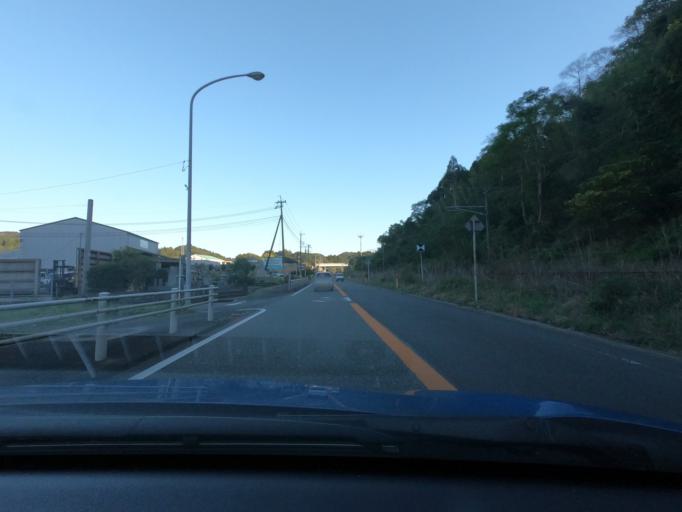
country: JP
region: Kagoshima
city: Satsumasendai
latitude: 31.8509
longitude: 130.2405
